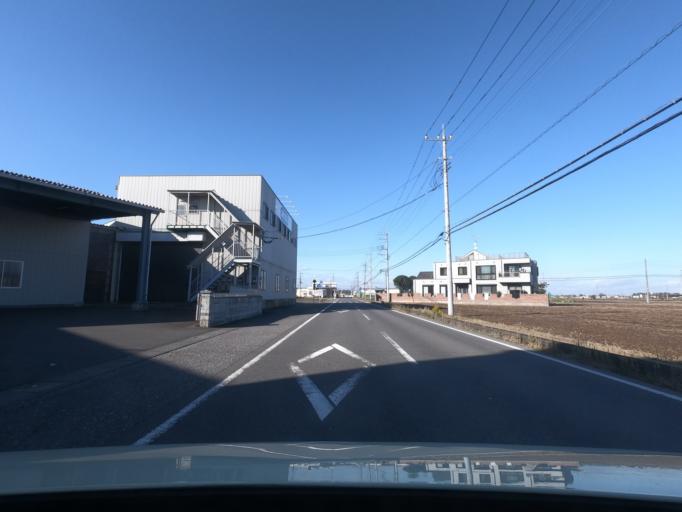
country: JP
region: Ibaraki
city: Ishige
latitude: 36.1630
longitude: 139.9925
